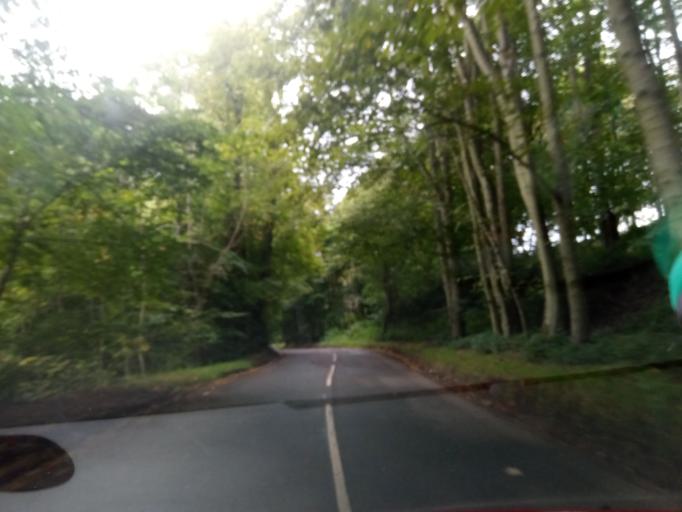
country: GB
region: Scotland
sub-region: The Scottish Borders
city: Duns
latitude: 55.8184
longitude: -2.3968
